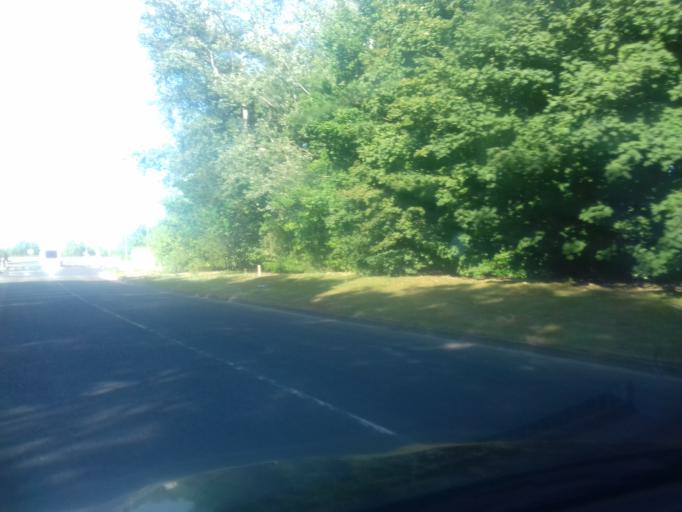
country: IE
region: Leinster
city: Hartstown
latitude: 53.4147
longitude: -6.4219
